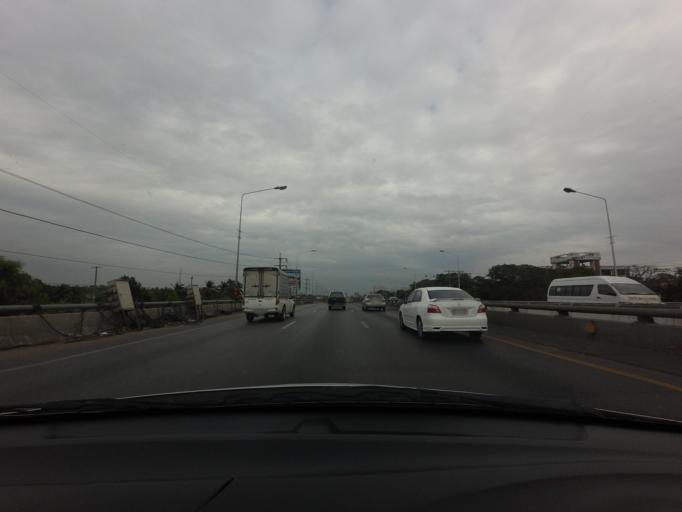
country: TH
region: Nakhon Pathom
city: Nakhon Chai Si
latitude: 13.7826
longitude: 100.2434
